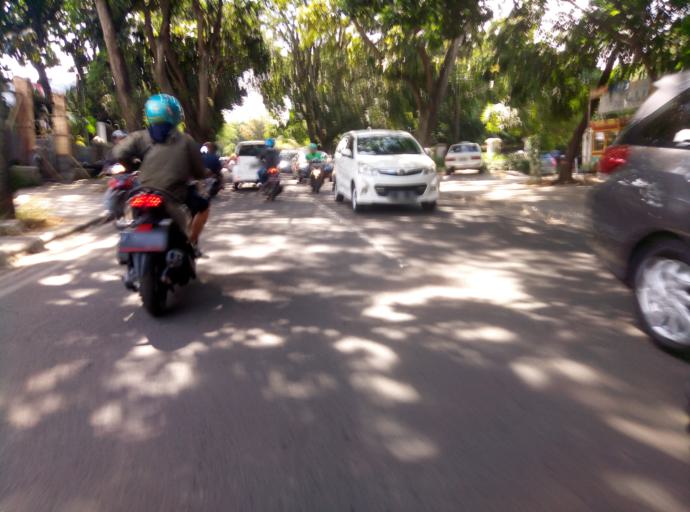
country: ID
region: West Java
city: Bandung
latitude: -6.8967
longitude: 107.6096
